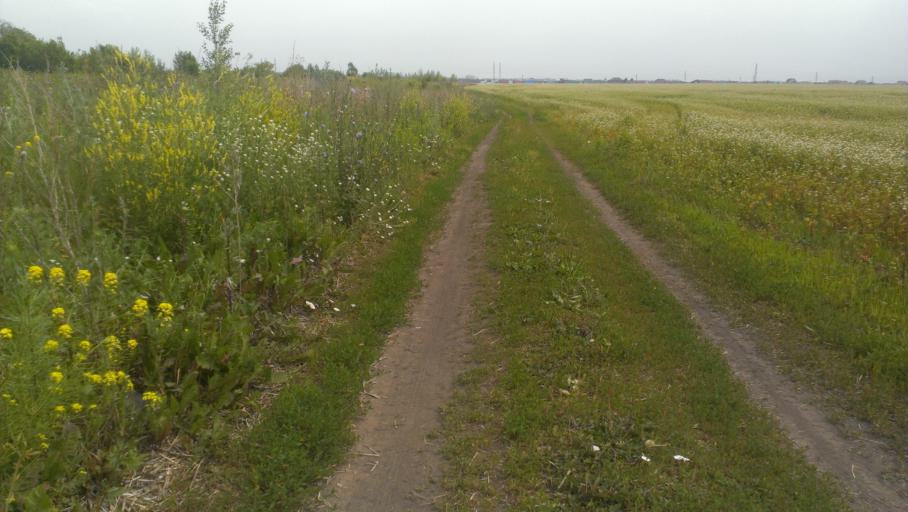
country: RU
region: Altai Krai
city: Novosilikatnyy
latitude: 53.3777
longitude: 83.6383
